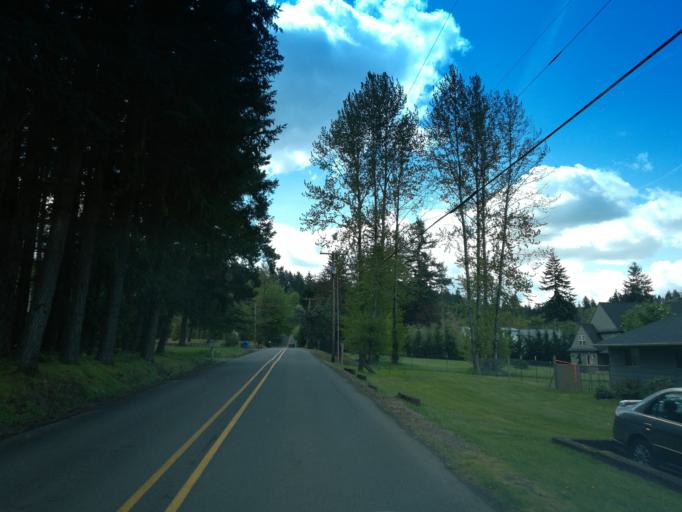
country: US
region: Oregon
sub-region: Clackamas County
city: Damascus
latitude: 45.4363
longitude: -122.4498
